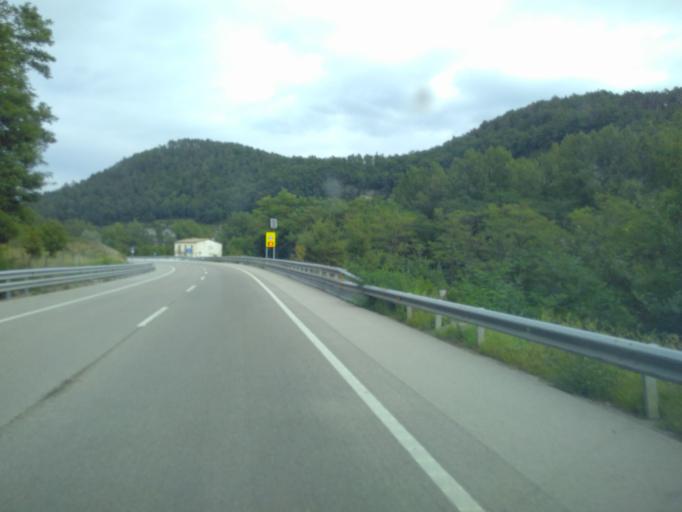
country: ES
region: Catalonia
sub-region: Provincia de Barcelona
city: Montesquiu
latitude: 42.1234
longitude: 2.2024
